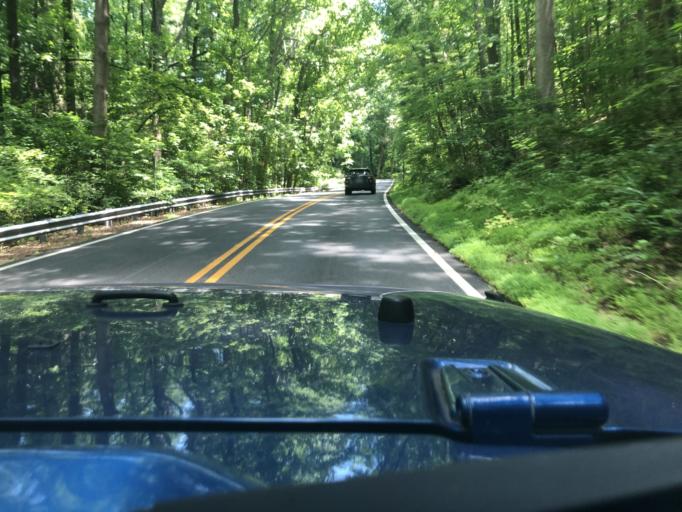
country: US
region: Maryland
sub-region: Baltimore County
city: Hampton
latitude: 39.4540
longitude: -76.5429
